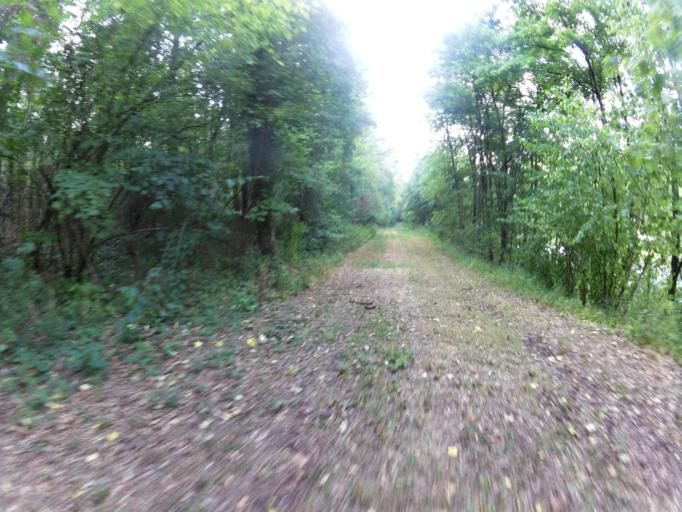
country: DE
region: Bavaria
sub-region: Regierungsbezirk Unterfranken
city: Ochsenfurt
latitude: 49.6549
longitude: 10.0728
